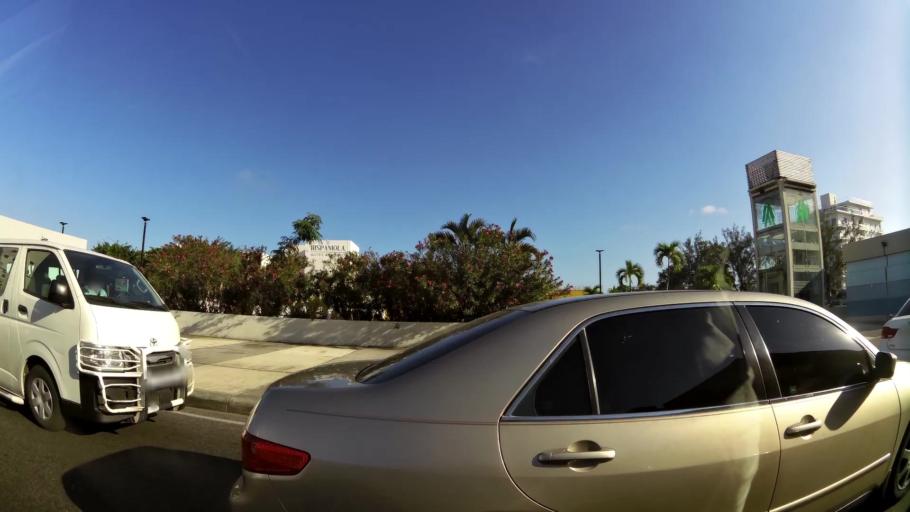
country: DO
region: Nacional
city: La Julia
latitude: 18.4557
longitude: -69.9238
